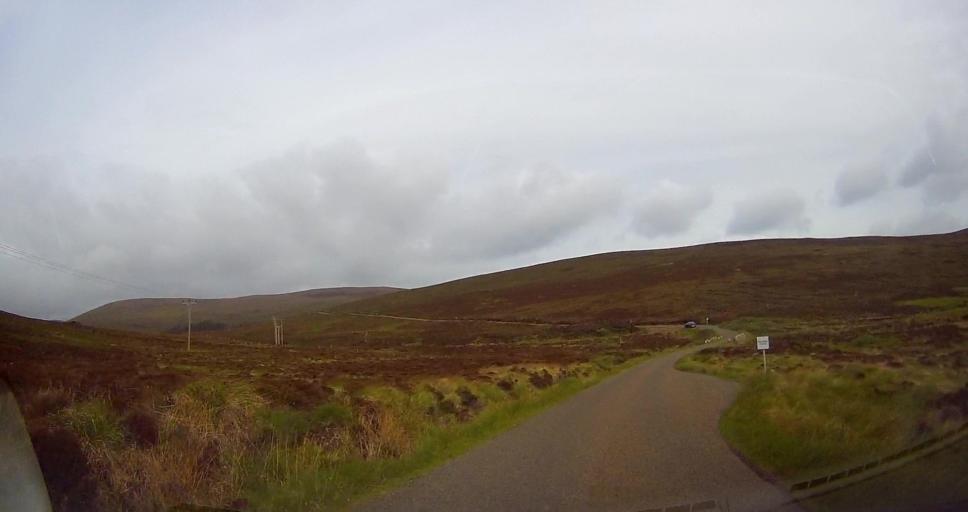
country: GB
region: Scotland
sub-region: Orkney Islands
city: Stromness
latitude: 58.8691
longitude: -3.2315
